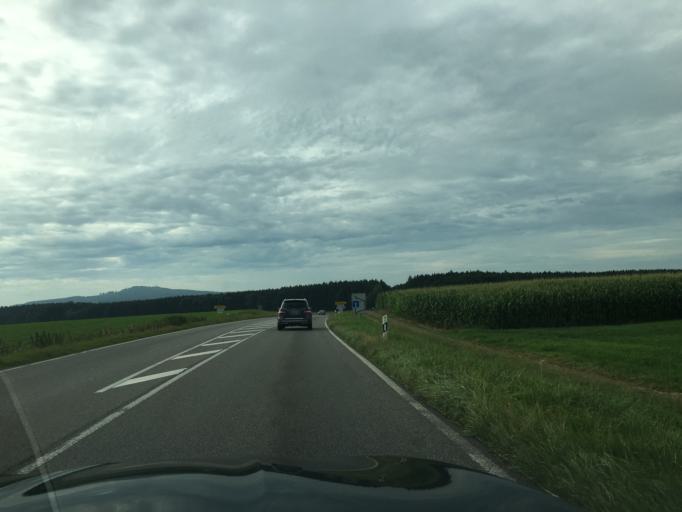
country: DE
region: Baden-Wuerttemberg
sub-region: Tuebingen Region
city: Emeringen
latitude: 48.2069
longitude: 9.5321
